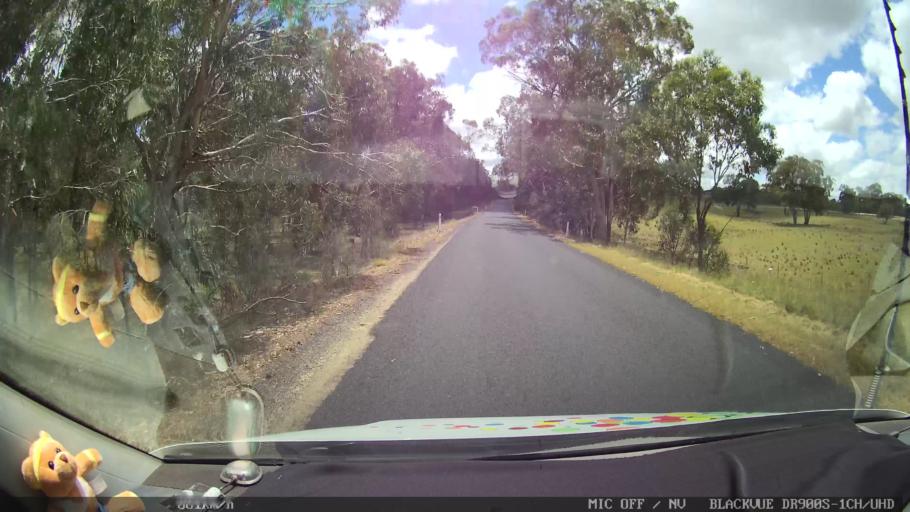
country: AU
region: New South Wales
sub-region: Glen Innes Severn
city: Glen Innes
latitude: -29.4293
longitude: 151.7936
